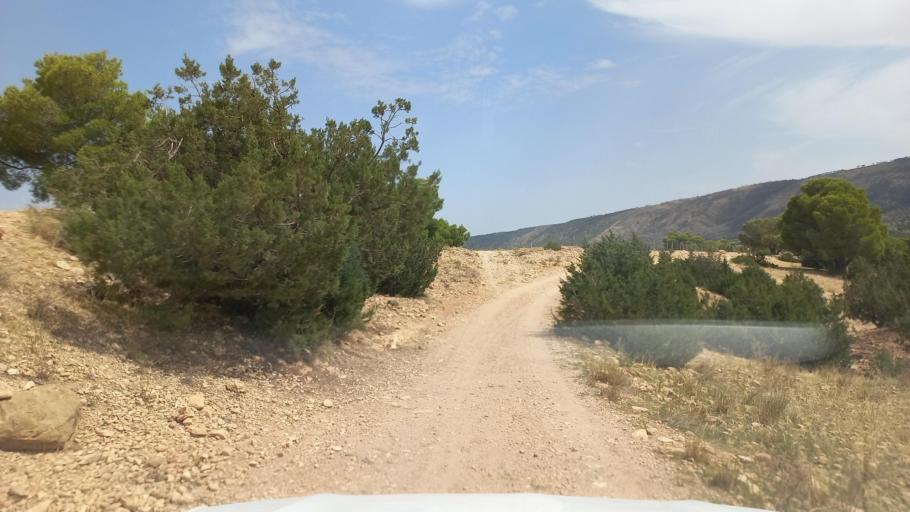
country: TN
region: Al Qasrayn
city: Kasserine
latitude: 35.3702
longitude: 8.8933
